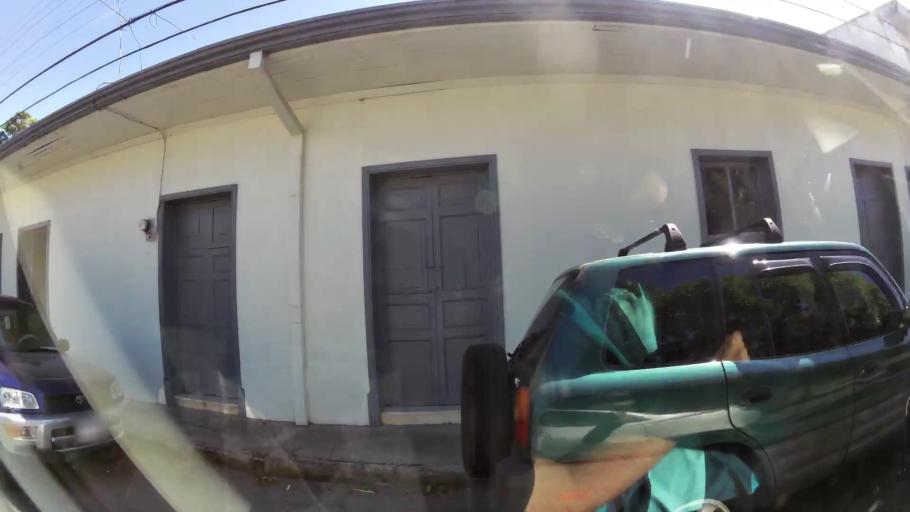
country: CR
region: Guanacaste
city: Liberia
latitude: 10.6291
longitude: -85.4362
